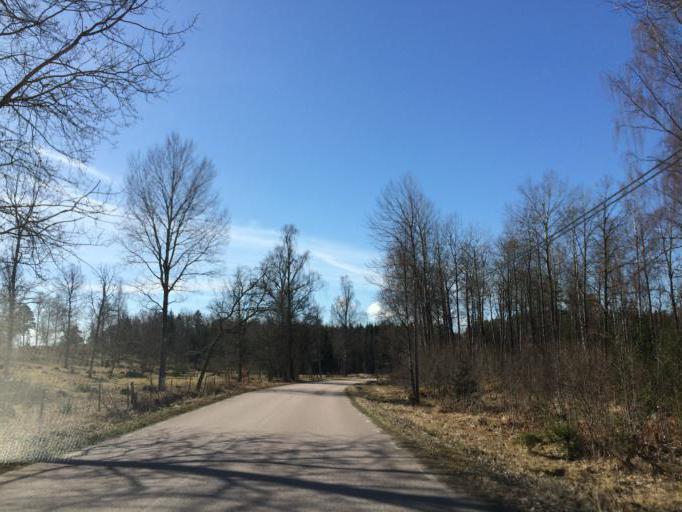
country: SE
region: Soedermanland
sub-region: Eskilstuna Kommun
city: Kvicksund
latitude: 59.5116
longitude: 16.2924
